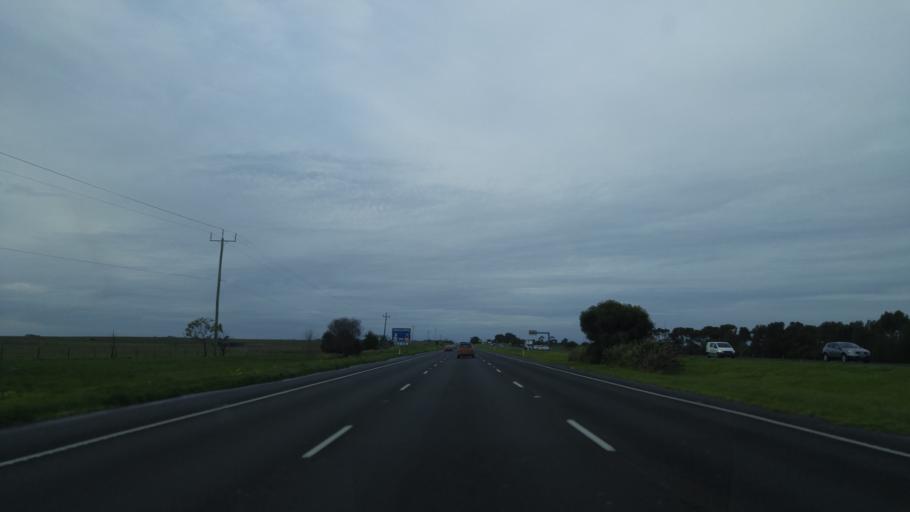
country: AU
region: Victoria
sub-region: Wyndham
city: Little River
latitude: -38.0082
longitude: 144.4785
